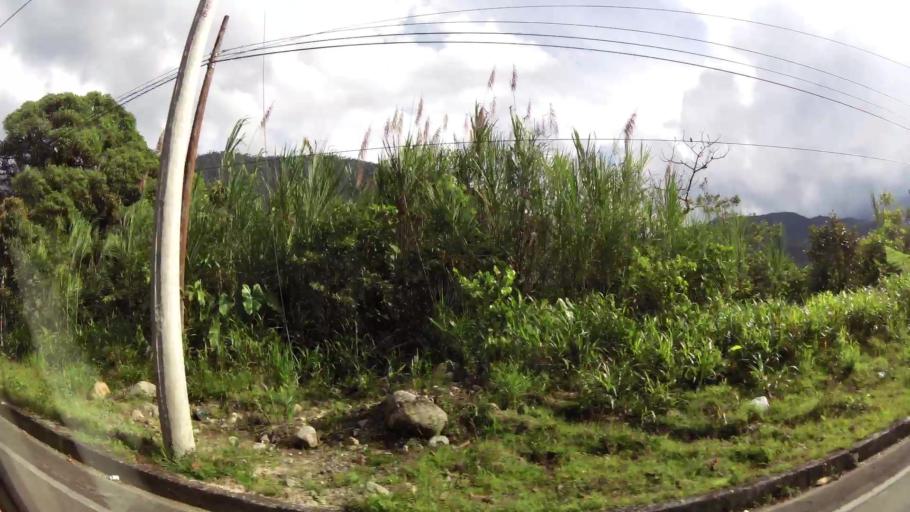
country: EC
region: Pastaza
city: Puyo
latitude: -1.4119
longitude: -78.1983
